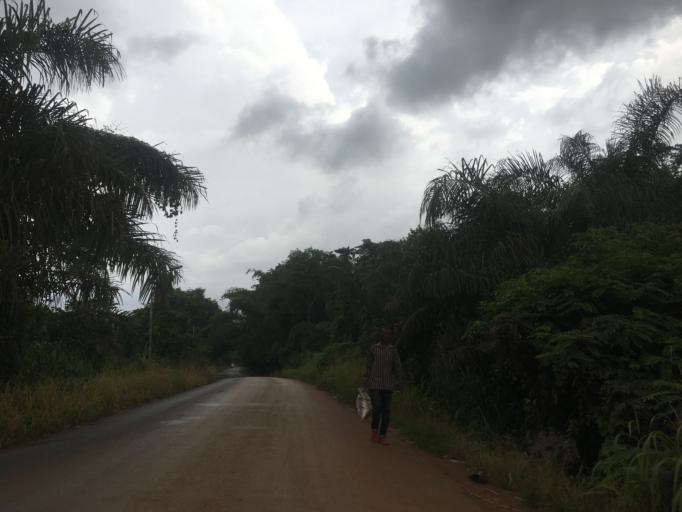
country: GH
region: Ashanti
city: Mamponteng
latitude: 6.6853
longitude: -1.5608
